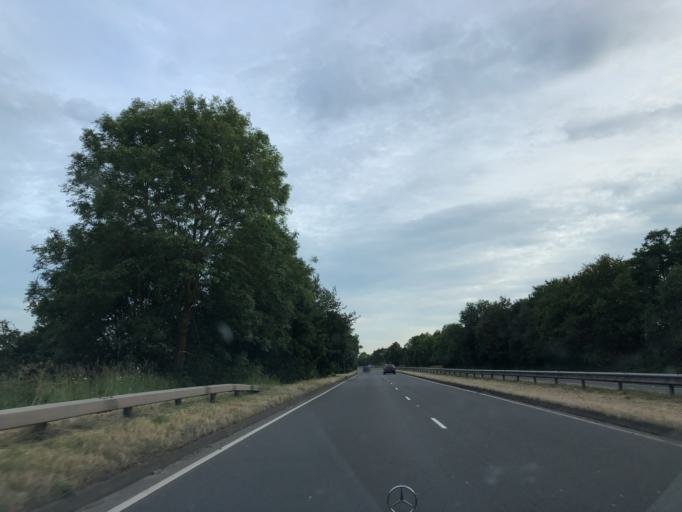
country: GB
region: England
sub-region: Solihull
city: Hampton in Arden
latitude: 52.4281
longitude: -1.6758
